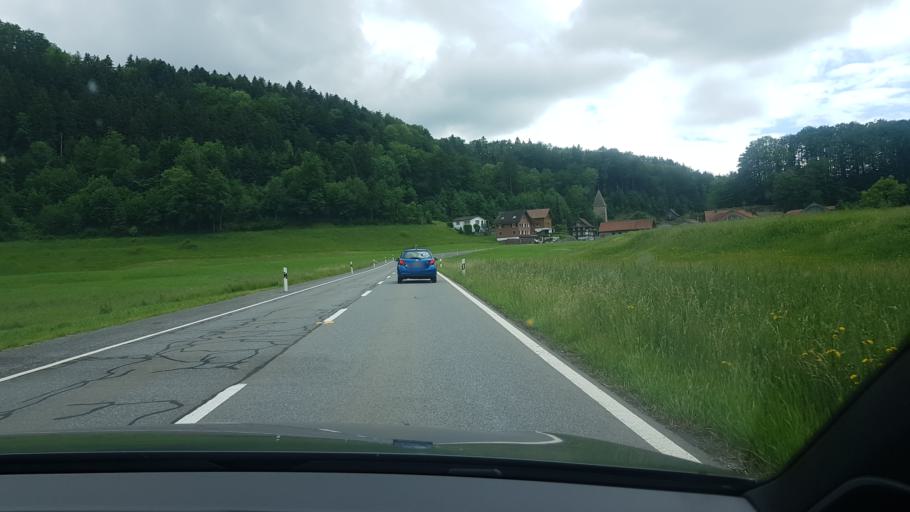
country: CH
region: Schwyz
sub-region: Bezirk Schwyz
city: Sattel
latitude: 47.0951
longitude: 8.6342
